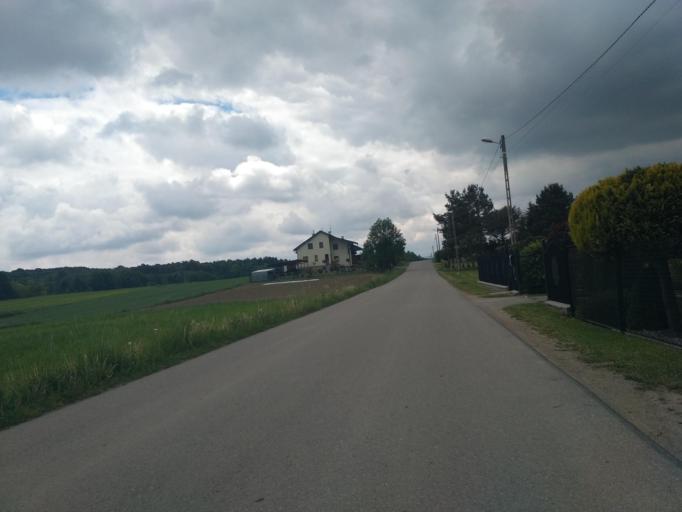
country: PL
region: Subcarpathian Voivodeship
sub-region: Powiat jasielski
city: Tarnowiec
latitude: 49.6661
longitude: 21.5655
